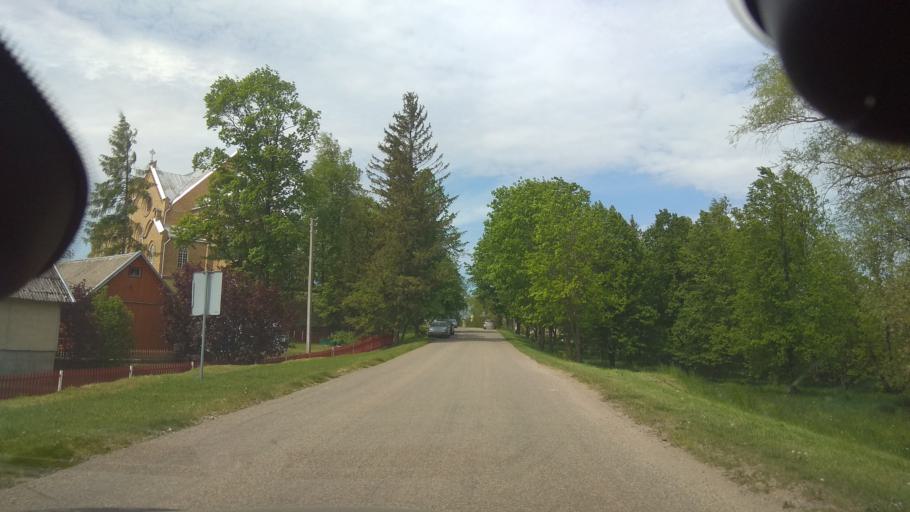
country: LT
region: Vilnius County
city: Ukmerge
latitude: 55.1494
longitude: 24.5771
